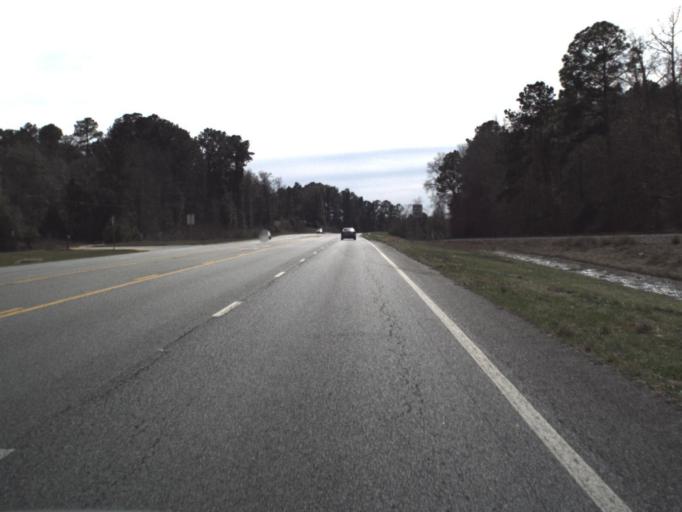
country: US
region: Florida
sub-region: Washington County
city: Chipley
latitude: 30.6593
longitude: -85.3933
